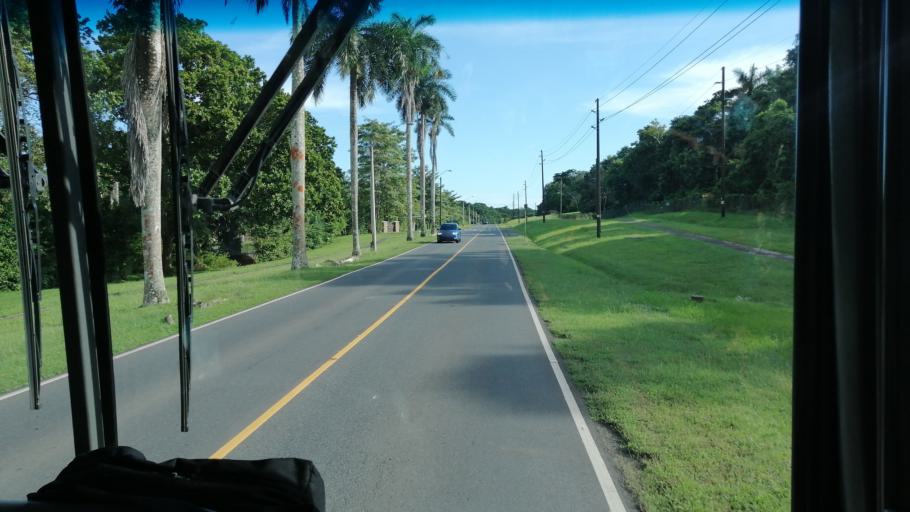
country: PA
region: Panama
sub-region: Distrito de Panama
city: Ancon
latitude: 8.9398
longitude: -79.5910
